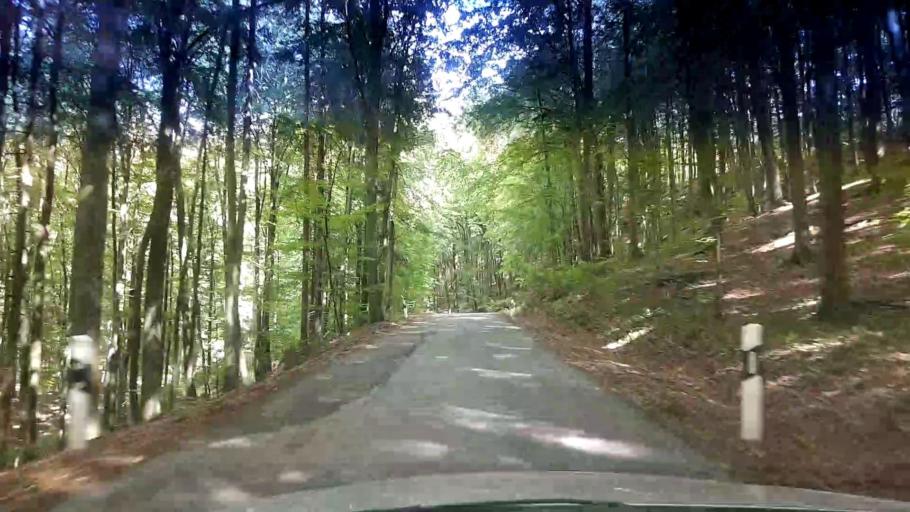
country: DE
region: Bavaria
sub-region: Upper Franconia
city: Schesslitz
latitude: 49.9511
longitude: 11.0673
